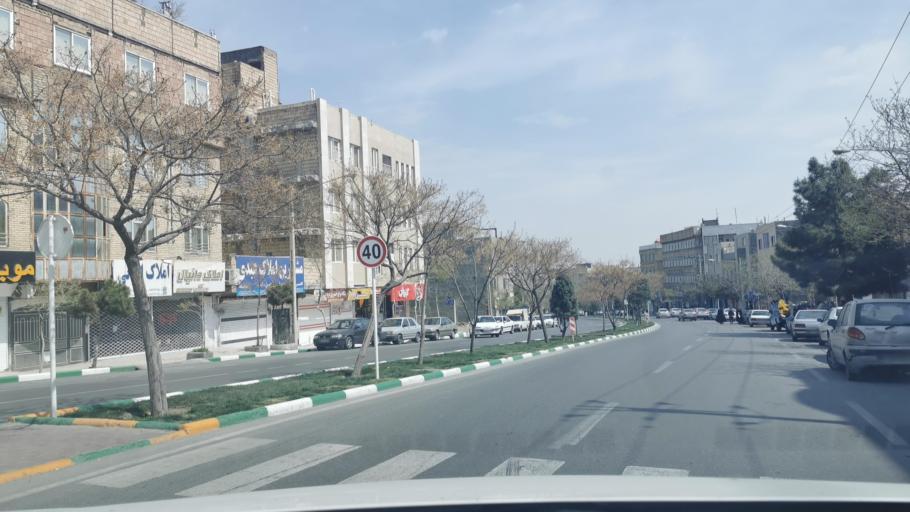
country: IR
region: Razavi Khorasan
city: Mashhad
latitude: 36.2900
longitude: 59.5033
